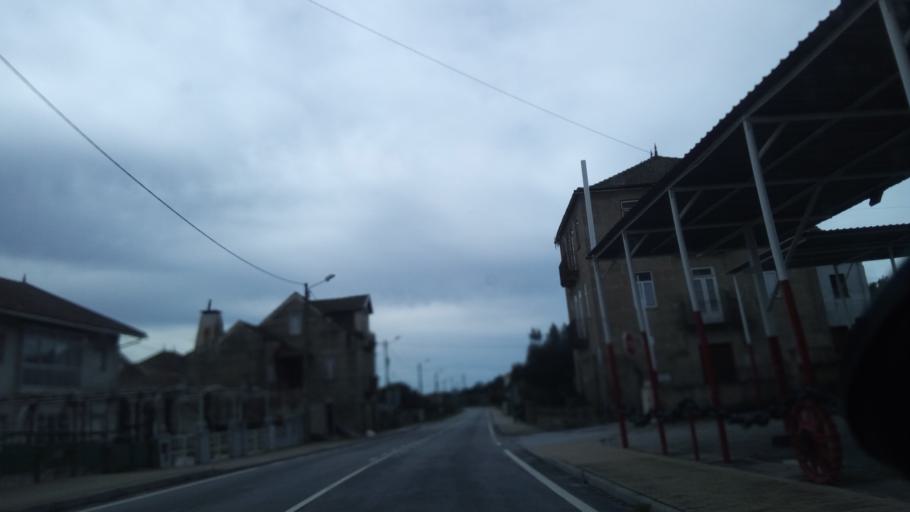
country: PT
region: Guarda
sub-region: Seia
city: Seia
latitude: 40.4658
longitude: -7.6843
